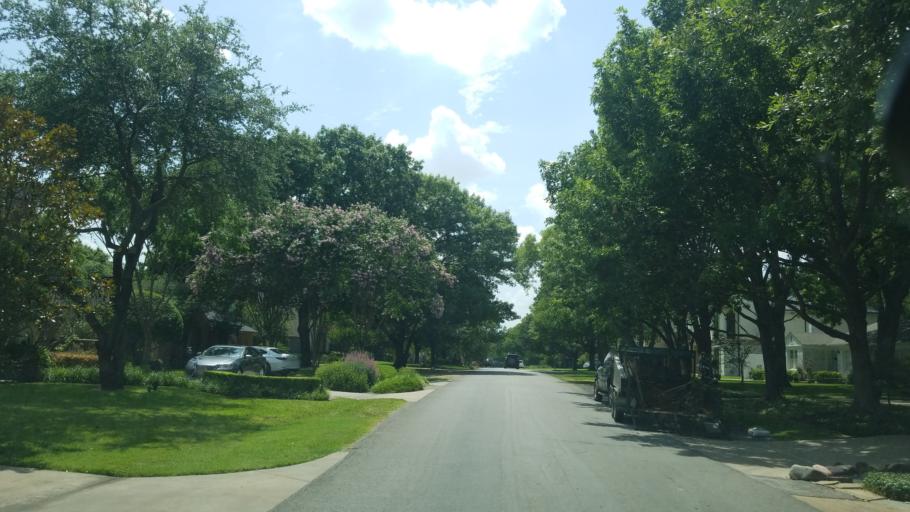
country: US
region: Texas
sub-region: Dallas County
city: University Park
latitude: 32.8695
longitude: -96.7960
